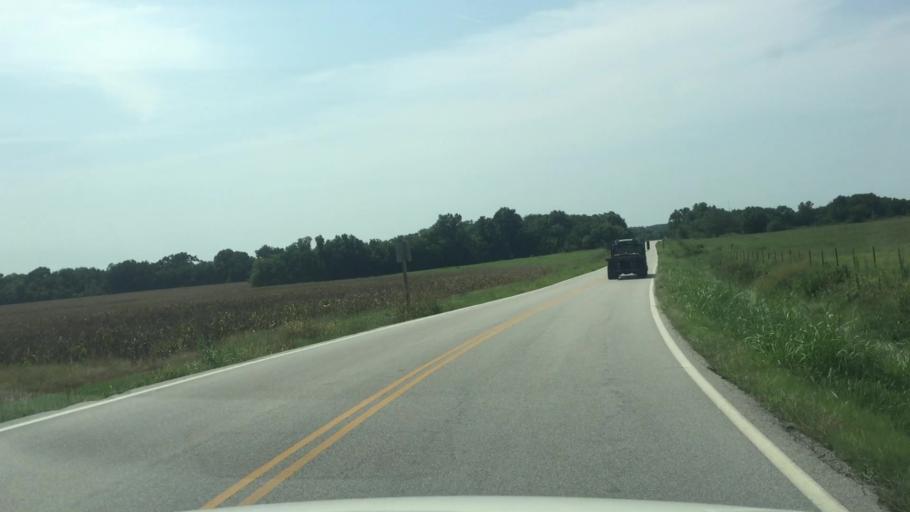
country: US
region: Kansas
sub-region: Montgomery County
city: Cherryvale
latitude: 37.2065
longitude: -95.5576
